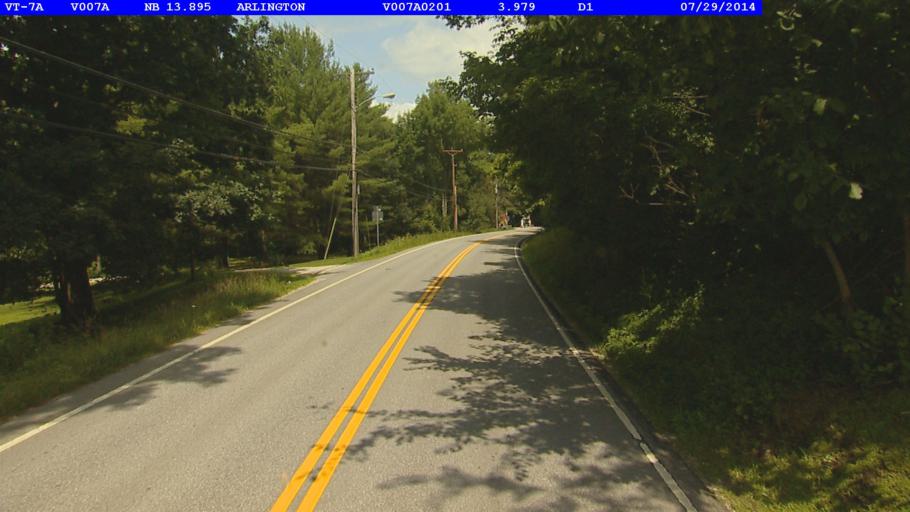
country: US
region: Vermont
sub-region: Bennington County
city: Arlington
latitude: 43.0761
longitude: -73.1538
